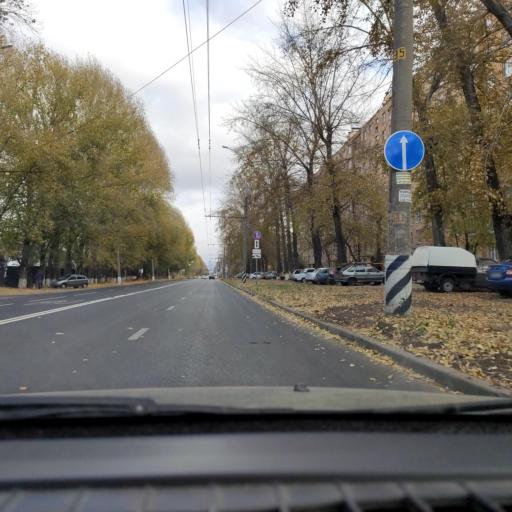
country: RU
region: Samara
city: Tol'yatti
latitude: 53.5383
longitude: 49.2742
